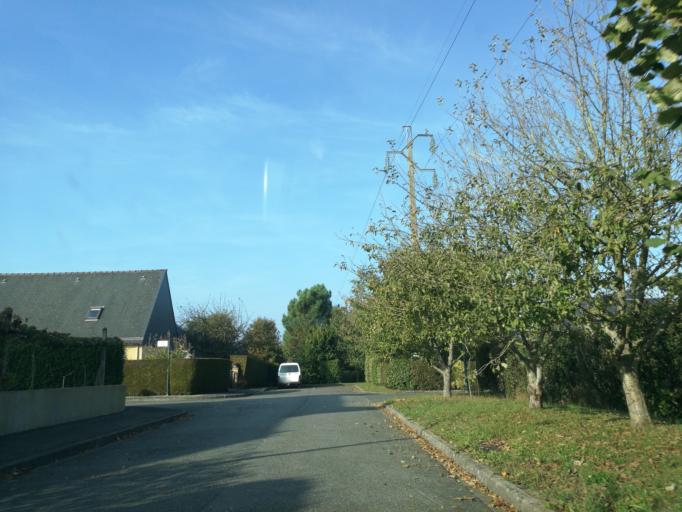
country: FR
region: Brittany
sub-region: Departement d'Ille-et-Vilaine
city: Breteil
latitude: 48.1490
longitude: -1.8979
